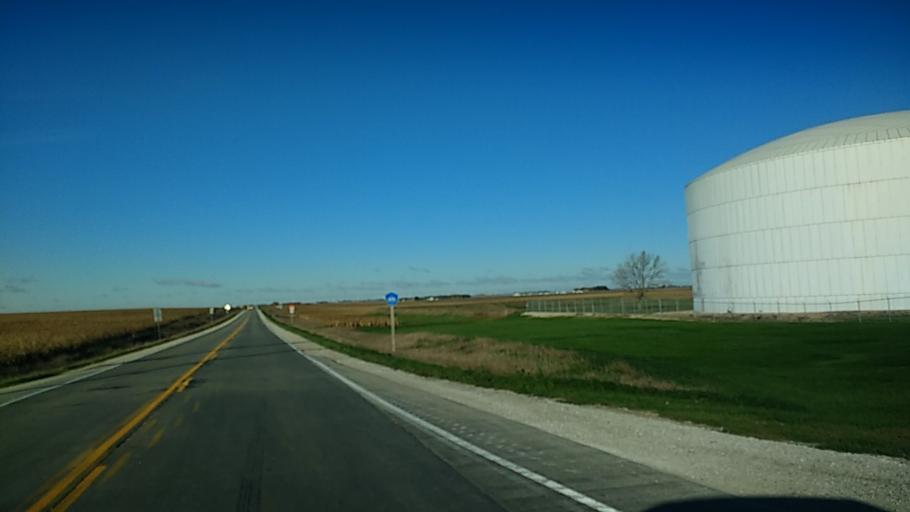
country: US
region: Iowa
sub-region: Buena Vista County
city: Storm Lake
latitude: 42.5181
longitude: -95.1512
